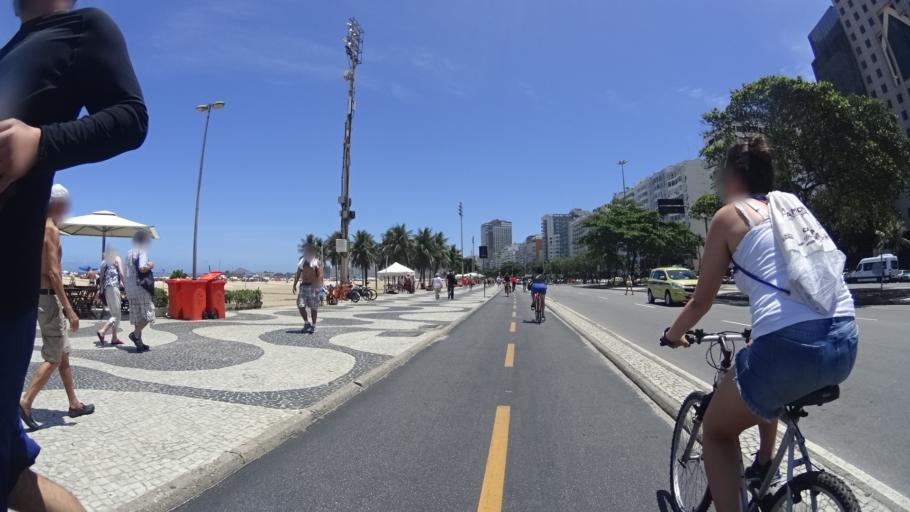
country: BR
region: Rio de Janeiro
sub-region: Rio De Janeiro
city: Rio de Janeiro
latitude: -22.9725
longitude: -43.1849
